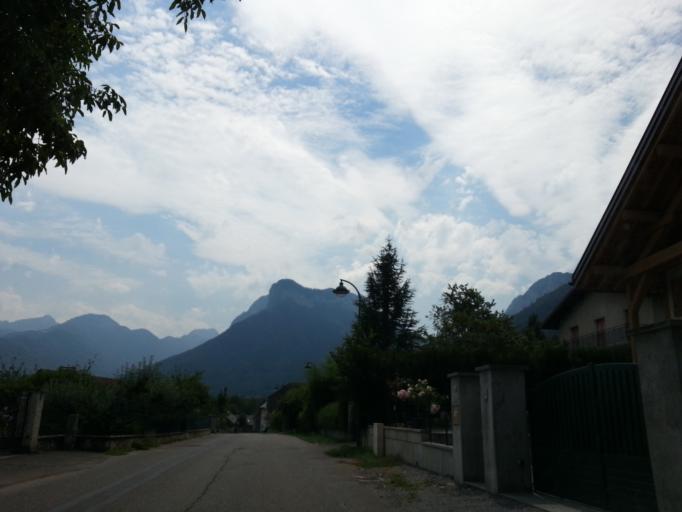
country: FR
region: Rhone-Alpes
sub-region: Departement de la Haute-Savoie
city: Doussard
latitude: 45.7893
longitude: 6.2032
